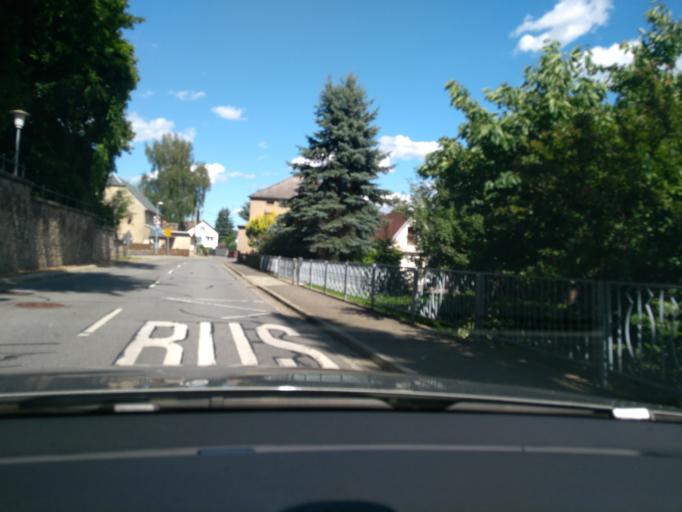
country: DE
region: Saxony
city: Demitz-Thumitz
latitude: 51.1378
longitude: 14.2424
